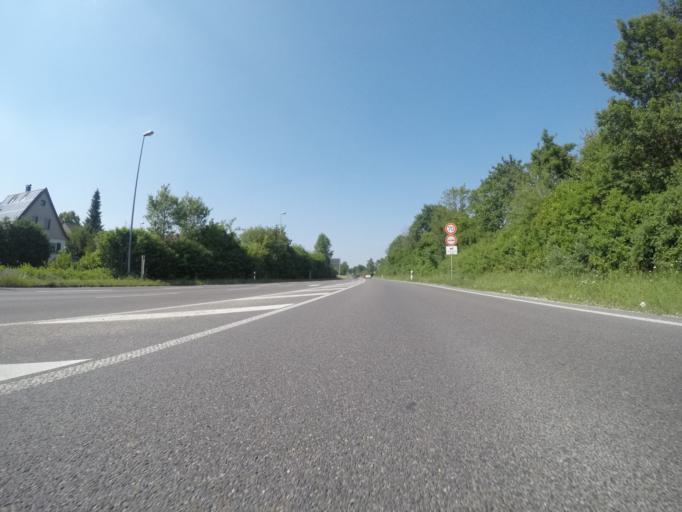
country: DE
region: Baden-Wuerttemberg
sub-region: Regierungsbezirk Stuttgart
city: Dettingen unter Teck
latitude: 48.6135
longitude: 9.4550
